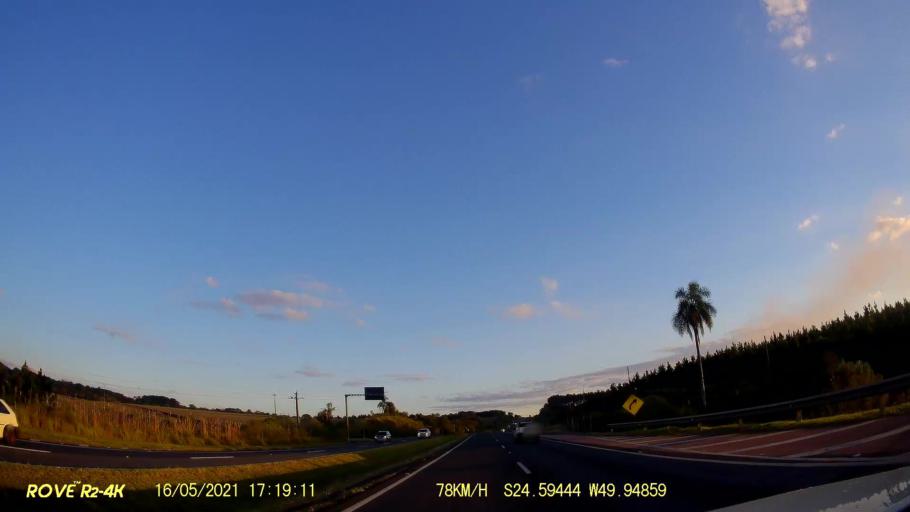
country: BR
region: Parana
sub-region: Pirai Do Sul
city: Pirai do Sul
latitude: -24.5947
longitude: -49.9487
